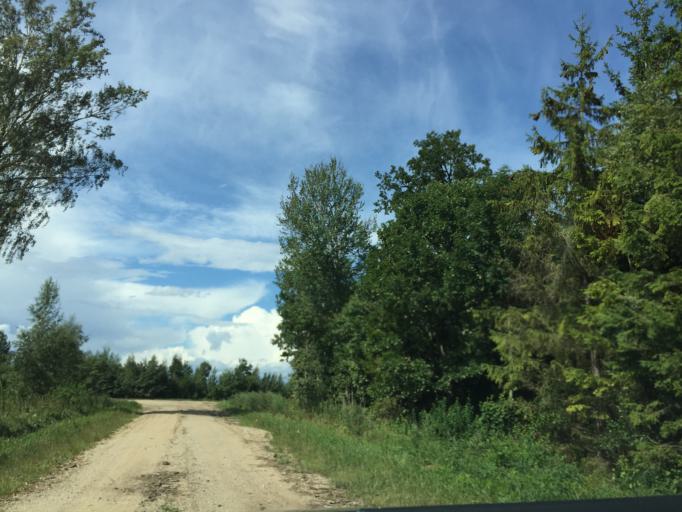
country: LT
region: Siauliu apskritis
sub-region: Joniskis
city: Joniskis
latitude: 56.3032
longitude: 23.6505
